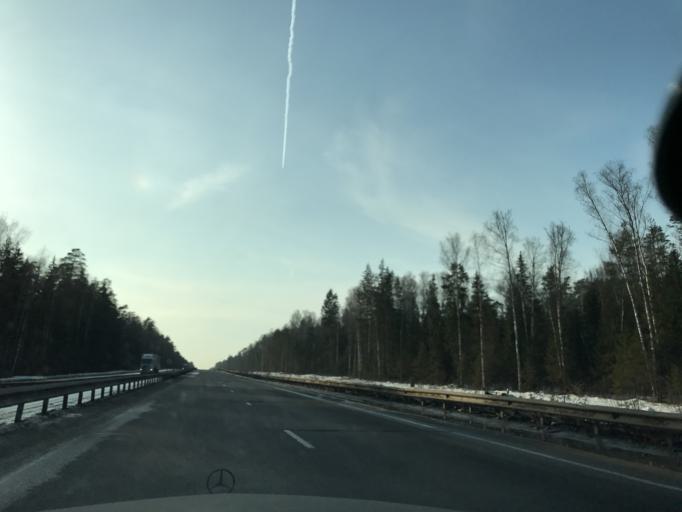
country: RU
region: Vladimir
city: Stepantsevo
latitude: 56.2276
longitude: 41.6695
